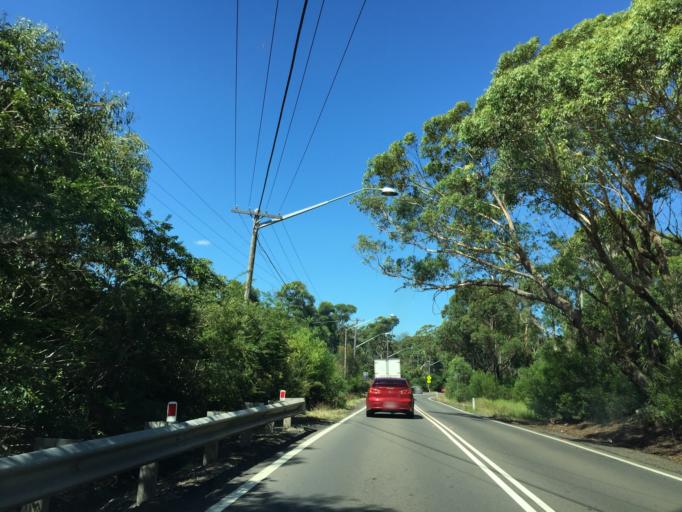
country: AU
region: New South Wales
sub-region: Willoughby
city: Chatswood West
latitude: -33.7961
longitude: 151.1482
